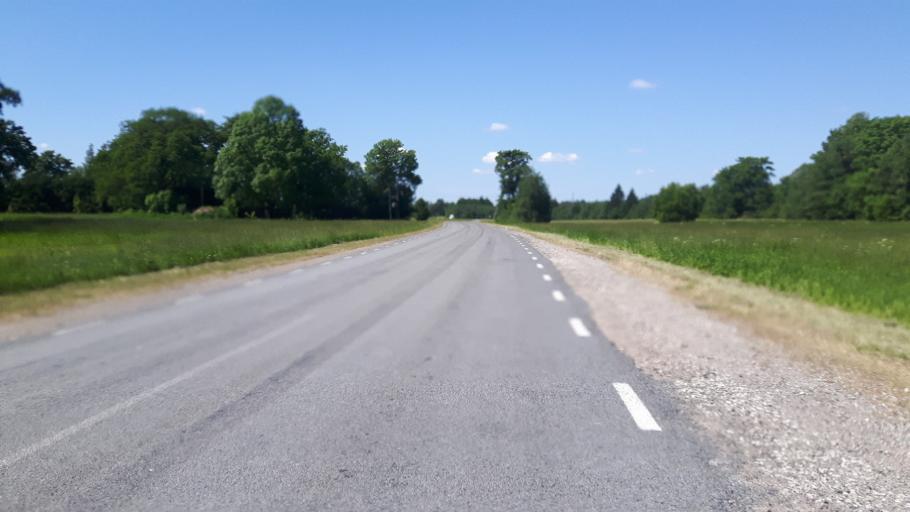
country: EE
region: Paernumaa
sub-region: Tootsi vald
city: Tootsi
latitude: 58.4958
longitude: 24.8849
